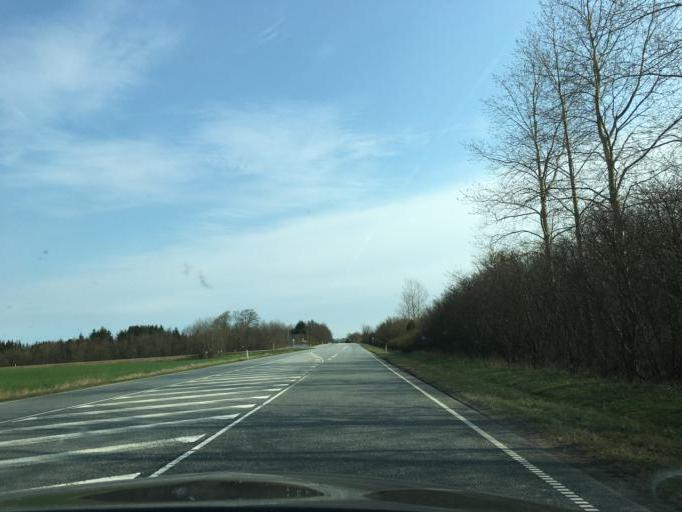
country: DK
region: South Denmark
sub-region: Kolding Kommune
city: Lunderskov
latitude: 55.4914
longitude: 9.2950
